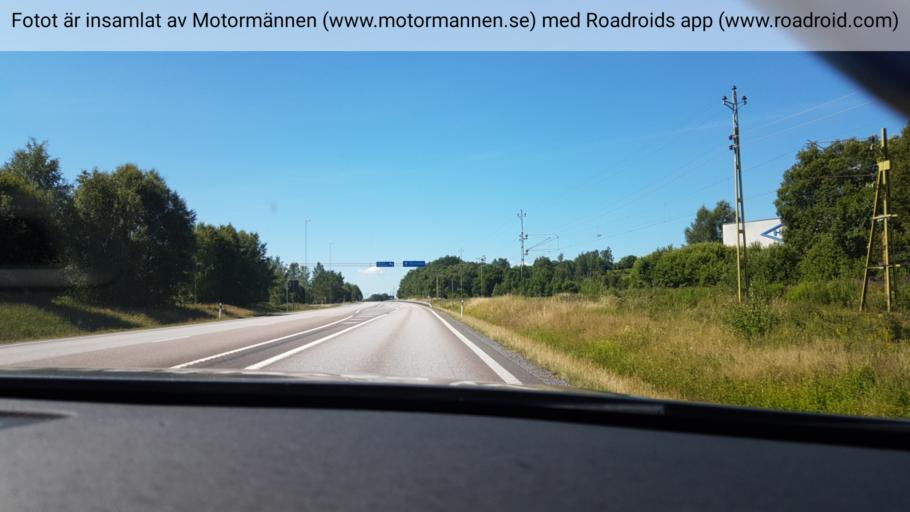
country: SE
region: Vaestra Goetaland
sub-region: Marks Kommun
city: Kinna
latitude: 57.4659
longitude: 12.5973
